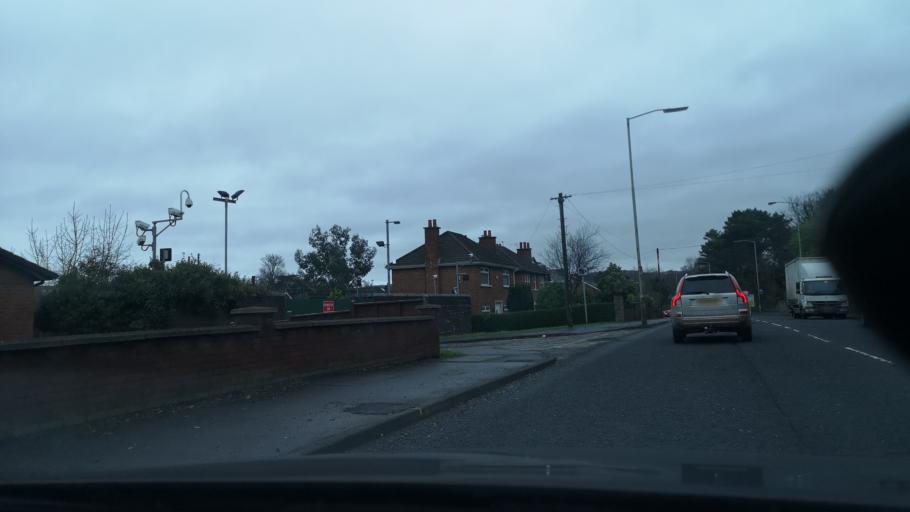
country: GB
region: Northern Ireland
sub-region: Castlereagh District
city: Castlereagh
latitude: 54.5871
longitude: -5.8586
